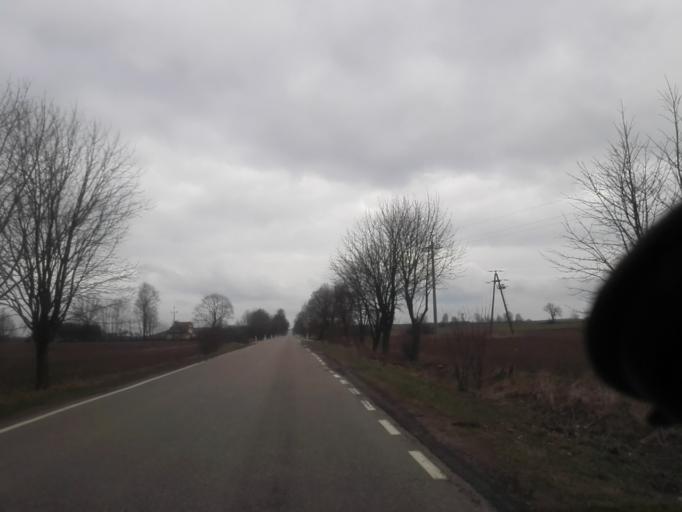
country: PL
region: Podlasie
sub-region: Suwalki
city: Suwalki
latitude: 54.2394
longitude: 22.9155
